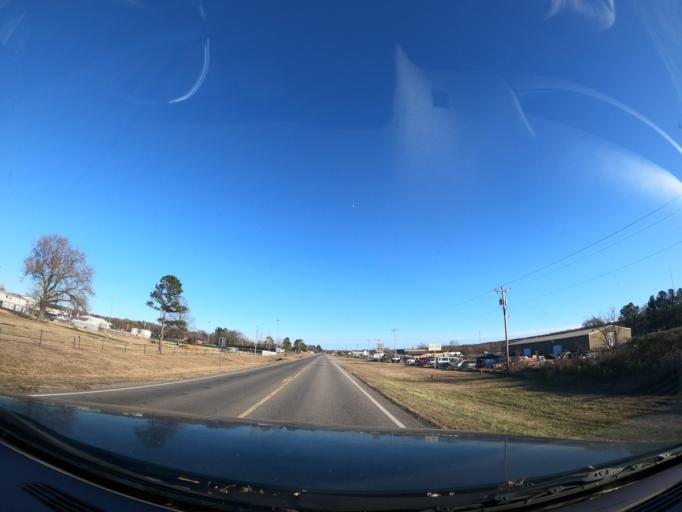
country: US
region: Oklahoma
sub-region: Latimer County
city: Wilburton
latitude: 34.9243
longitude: -95.3303
